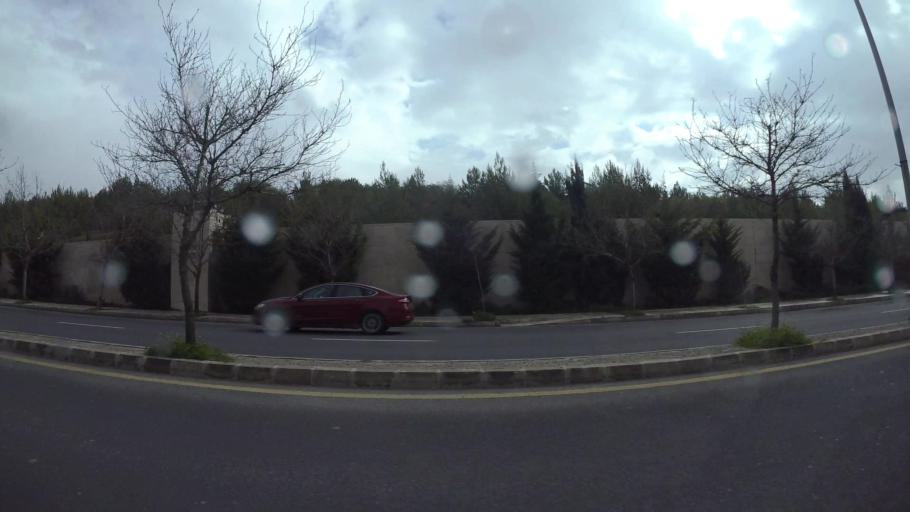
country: JO
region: Amman
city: Wadi as Sir
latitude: 31.9836
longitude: 35.8211
